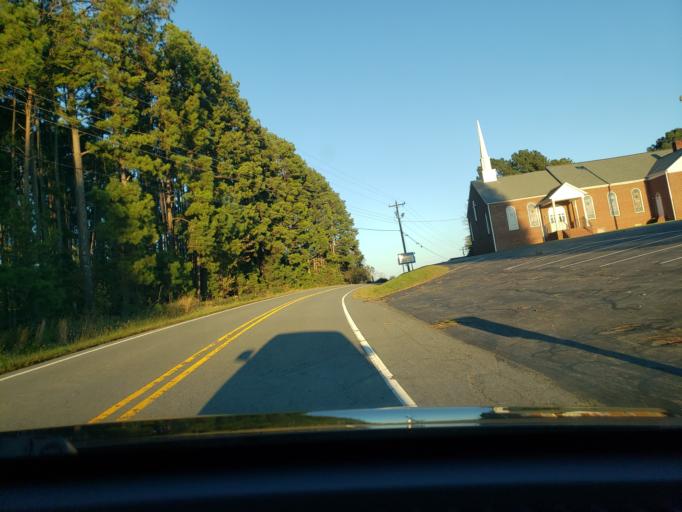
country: US
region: North Carolina
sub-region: Stokes County
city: Danbury
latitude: 36.3670
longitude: -80.1957
